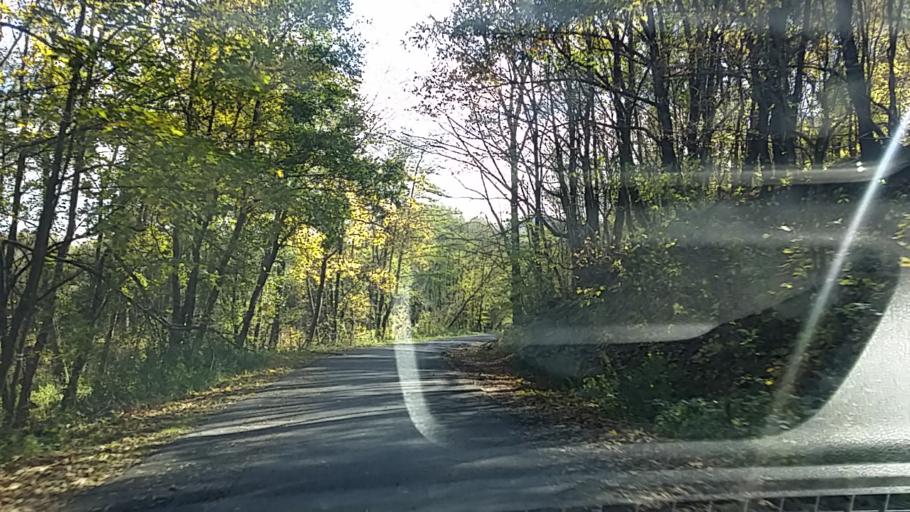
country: HU
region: Borsod-Abauj-Zemplen
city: Gonc
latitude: 48.3944
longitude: 21.3535
